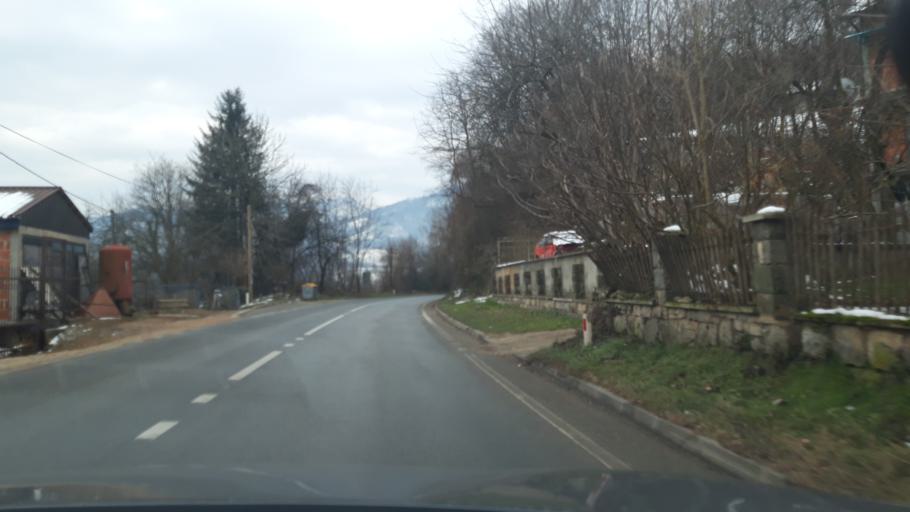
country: RS
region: Central Serbia
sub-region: Macvanski Okrug
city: Mali Zvornik
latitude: 44.2979
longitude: 19.1494
